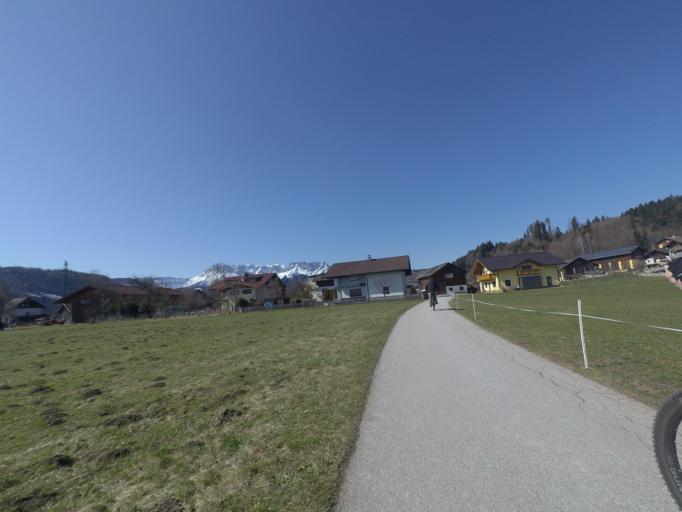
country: AT
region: Salzburg
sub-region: Politischer Bezirk Hallein
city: Adnet
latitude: 47.6734
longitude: 13.1299
